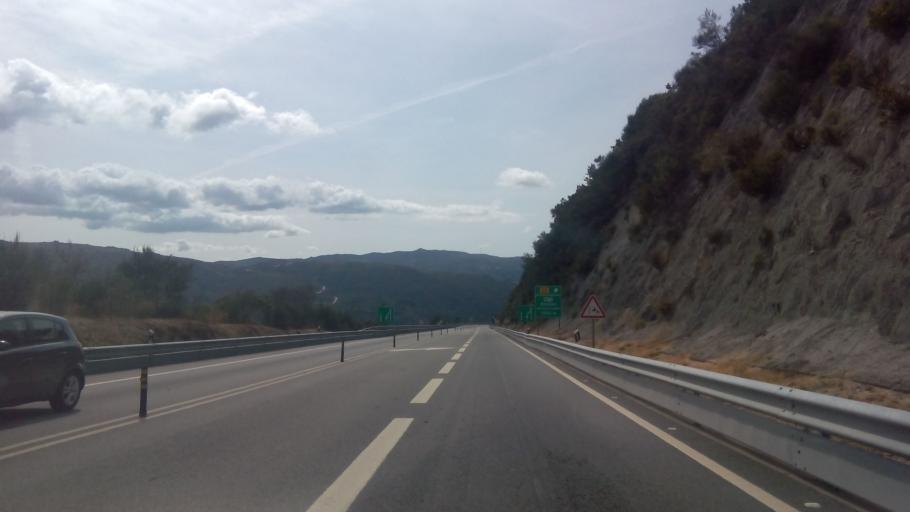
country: PT
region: Porto
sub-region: Baiao
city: Valadares
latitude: 41.2579
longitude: -7.9535
